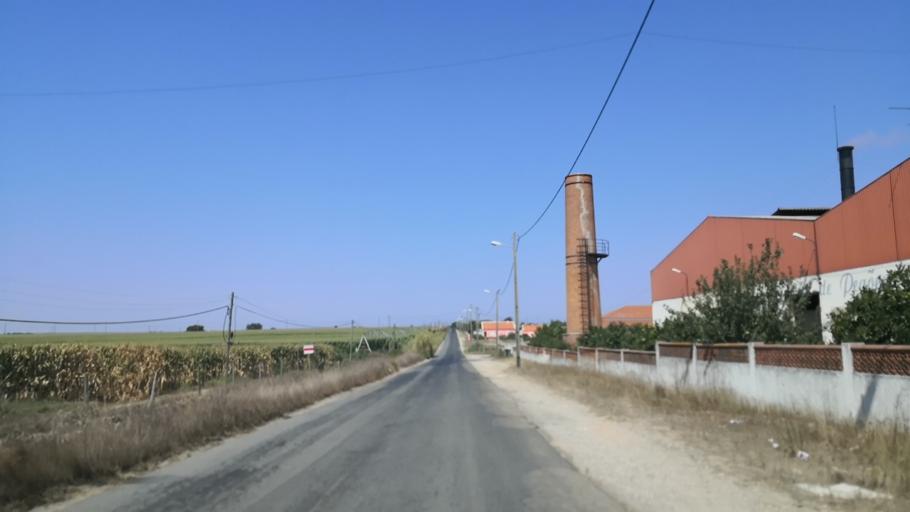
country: PT
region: Santarem
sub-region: Benavente
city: Poceirao
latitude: 38.7027
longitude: -8.7220
